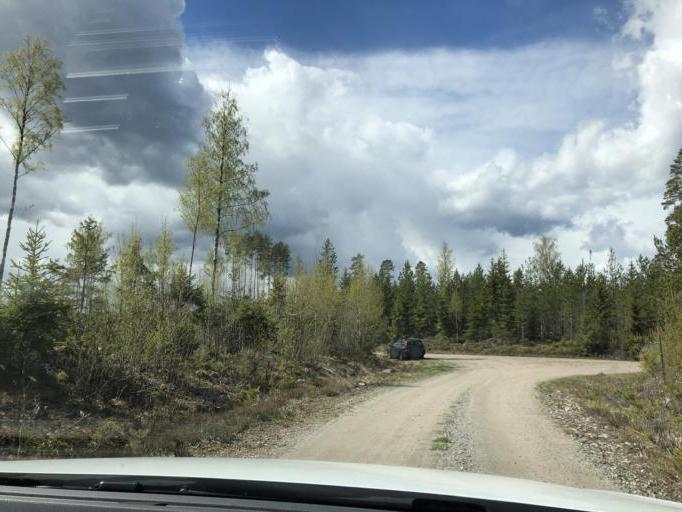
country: SE
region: Uppsala
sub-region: Heby Kommun
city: Tarnsjo
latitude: 60.2362
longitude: 16.8936
